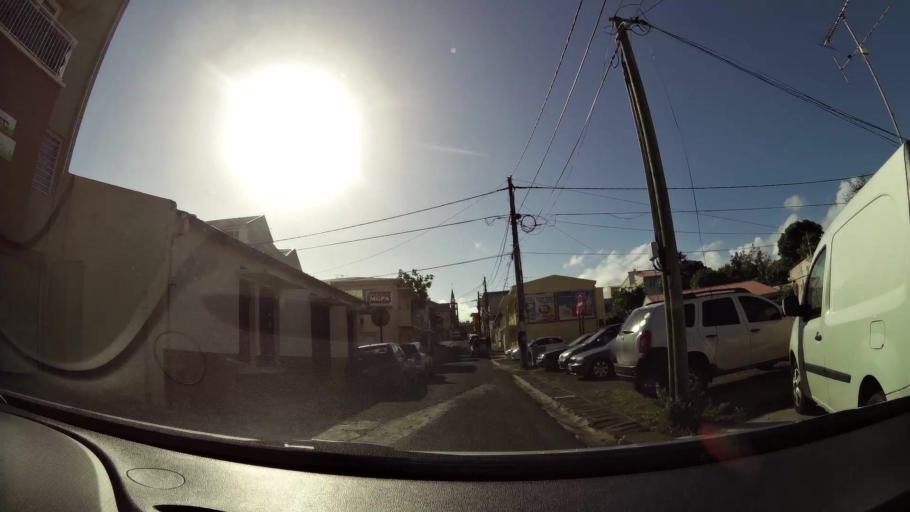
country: MQ
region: Martinique
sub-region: Martinique
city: Le Francois
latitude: 14.6163
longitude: -60.9039
